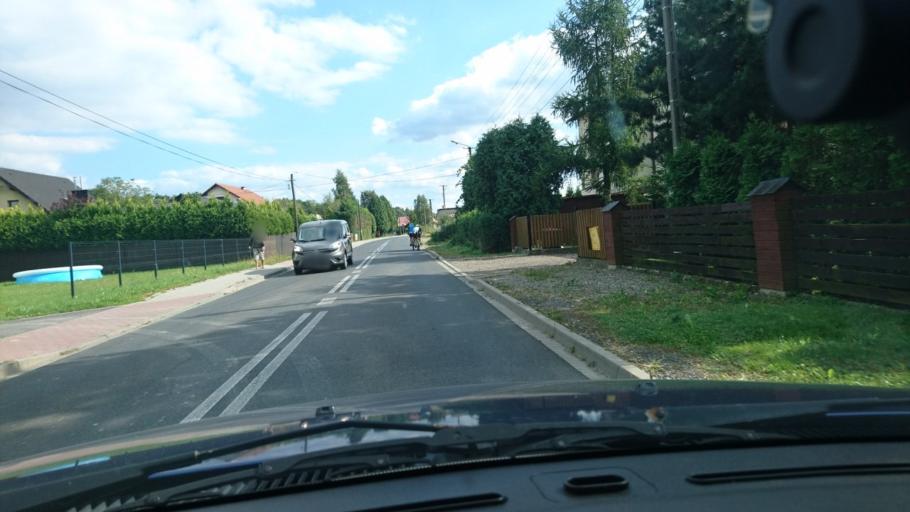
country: PL
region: Silesian Voivodeship
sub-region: Powiat bielski
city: Mazancowice
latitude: 49.8669
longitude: 18.9682
